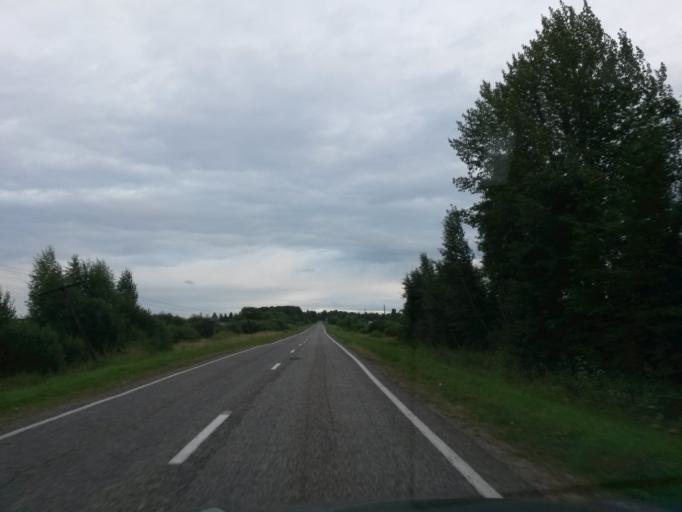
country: RU
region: Jaroslavl
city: Tutayev
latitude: 57.9061
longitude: 39.5212
